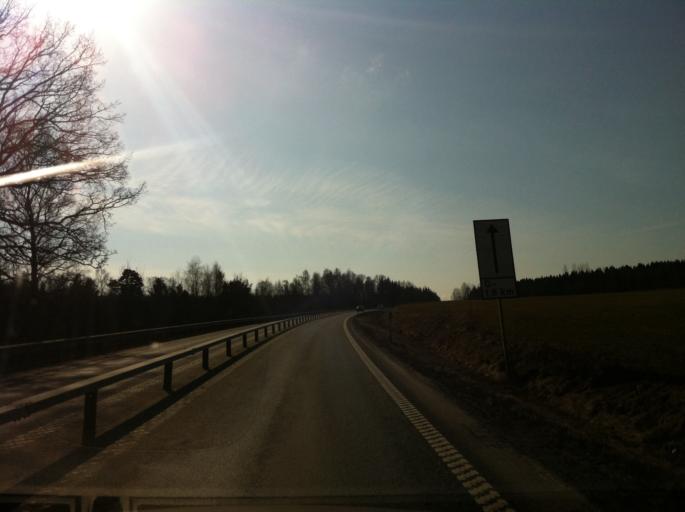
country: SE
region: Joenkoeping
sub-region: Jonkopings Kommun
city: Bankeryd
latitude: 57.8417
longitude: 14.1071
